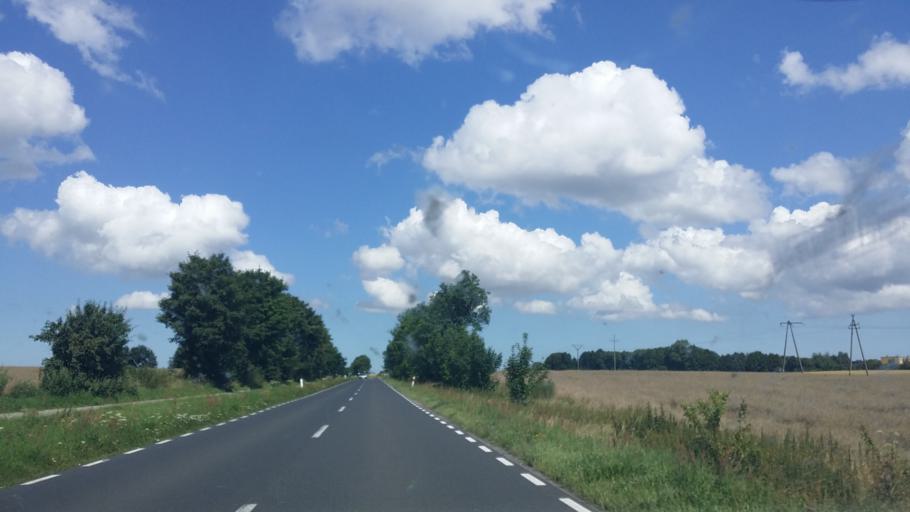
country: PL
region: West Pomeranian Voivodeship
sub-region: Powiat kolobrzeski
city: Goscino
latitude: 54.0355
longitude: 15.6585
